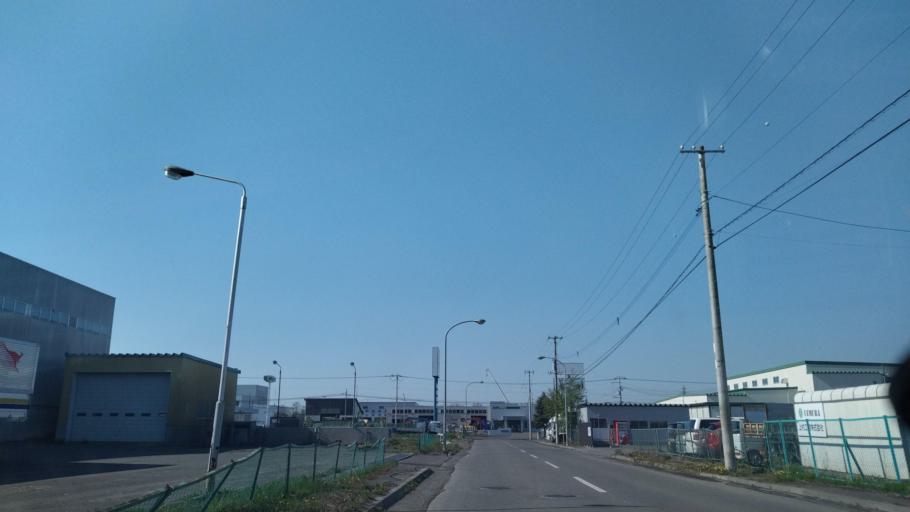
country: JP
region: Hokkaido
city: Obihiro
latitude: 42.9248
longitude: 143.0861
